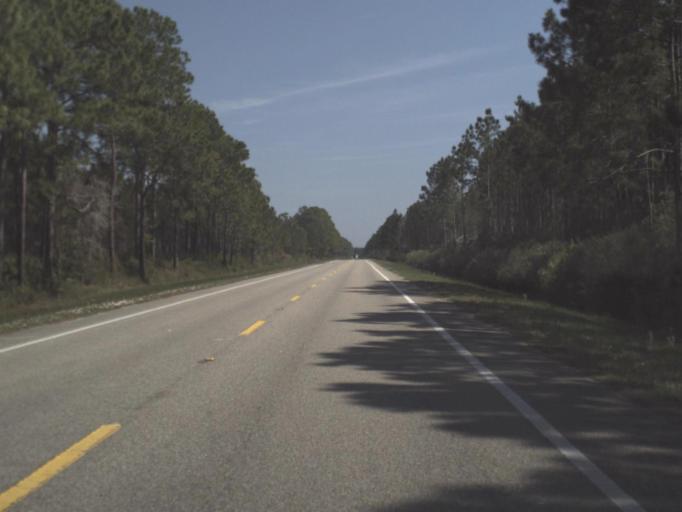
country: US
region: Florida
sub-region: Franklin County
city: Apalachicola
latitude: 29.7273
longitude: -85.1297
